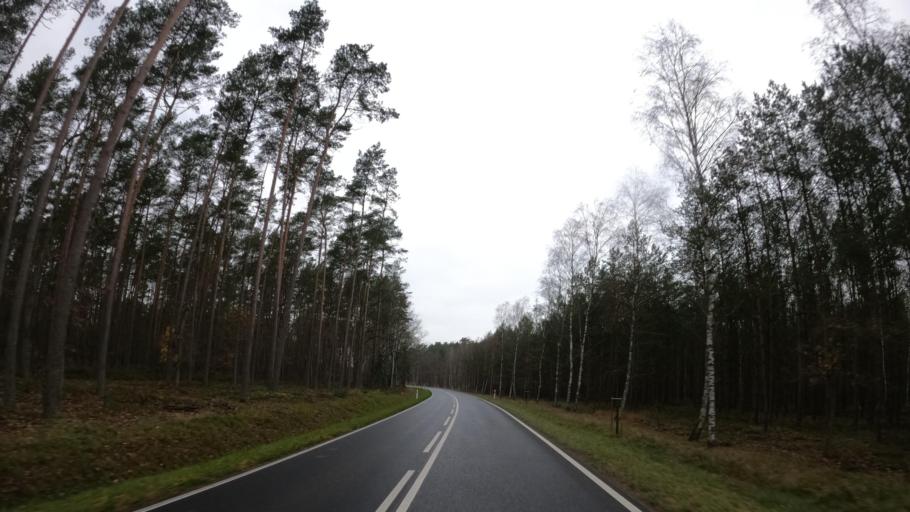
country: PL
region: West Pomeranian Voivodeship
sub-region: Powiat policki
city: Police
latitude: 53.6634
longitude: 14.4615
